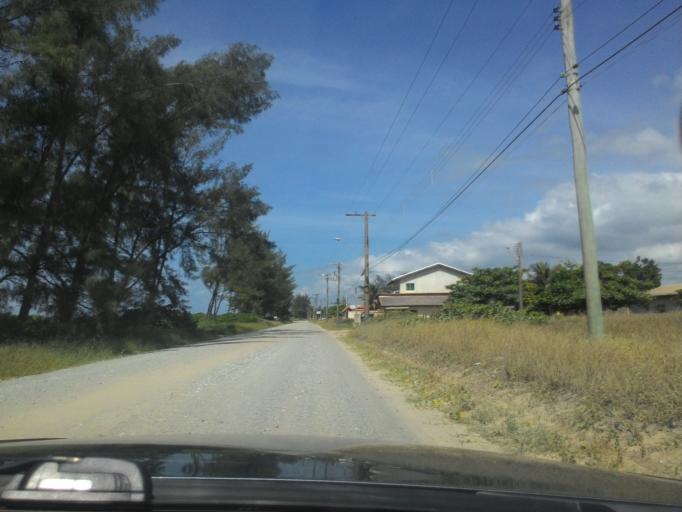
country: BR
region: Sao Paulo
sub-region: Iguape
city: Iguape
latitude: -24.8453
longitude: -47.6880
